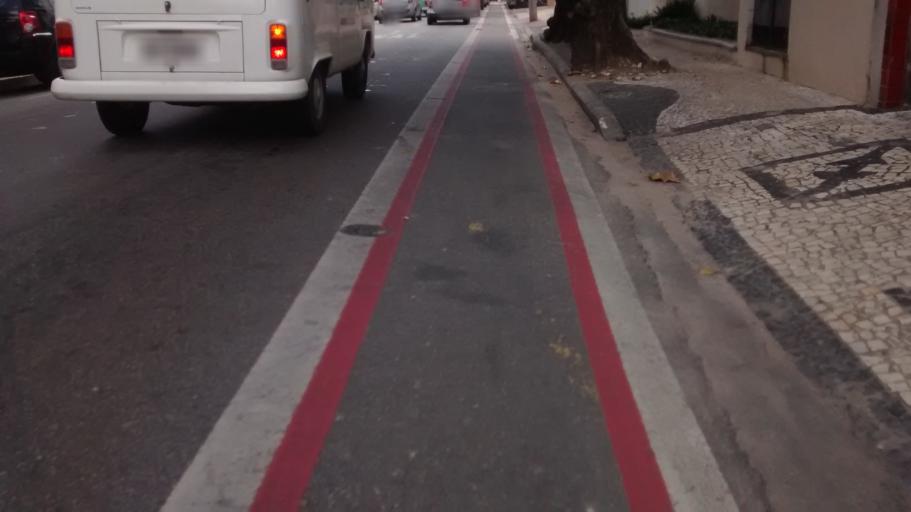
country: BR
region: Ceara
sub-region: Fortaleza
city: Fortaleza
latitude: -3.7332
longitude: -38.5108
